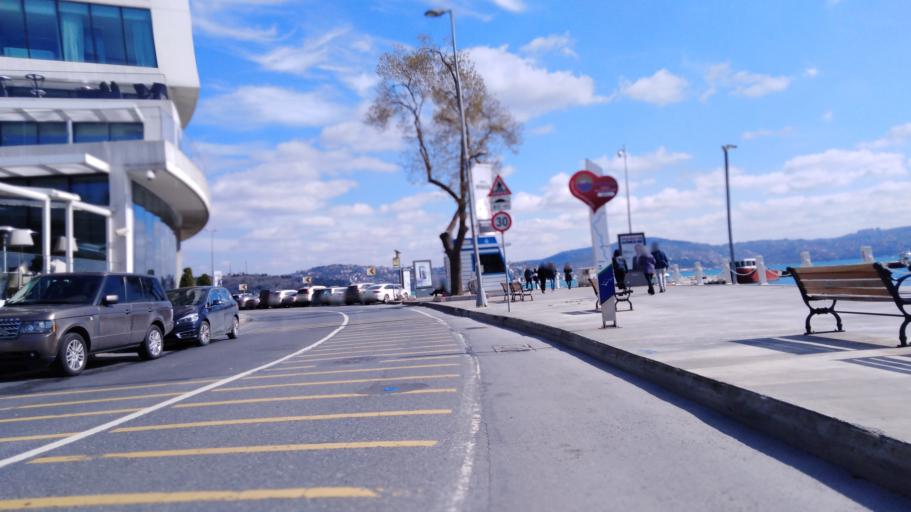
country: TR
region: Istanbul
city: Sisli
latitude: 41.1392
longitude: 29.0568
